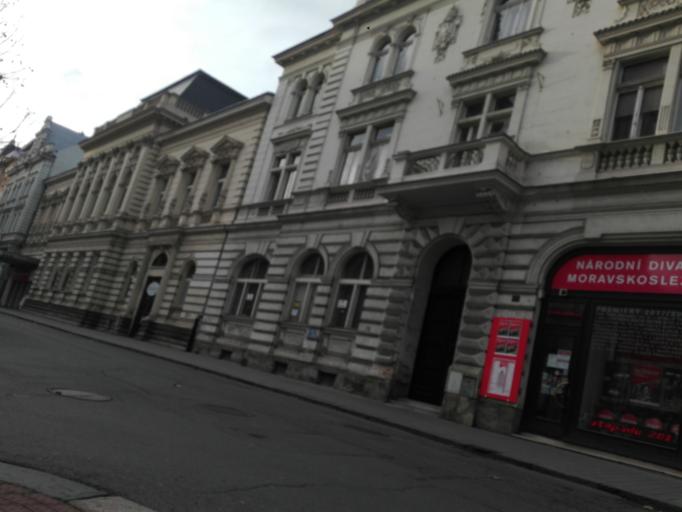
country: CZ
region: Moravskoslezsky
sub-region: Okres Ostrava-Mesto
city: Ostrava
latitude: 49.8364
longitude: 18.2889
